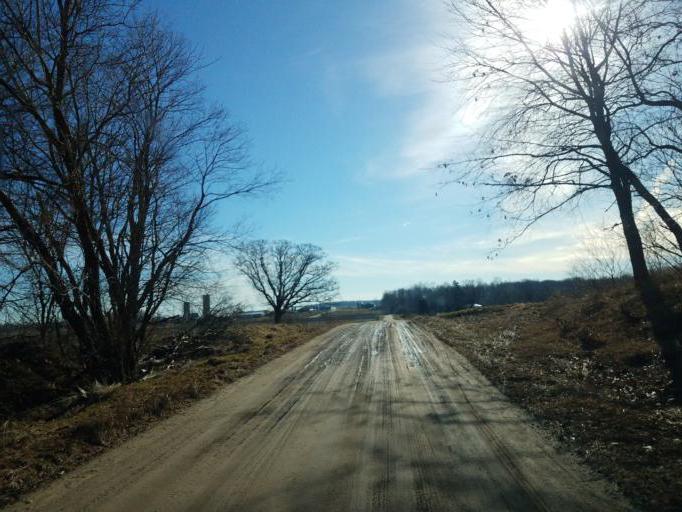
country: US
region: Michigan
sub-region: Montcalm County
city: Edmore
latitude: 43.4949
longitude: -85.0705
